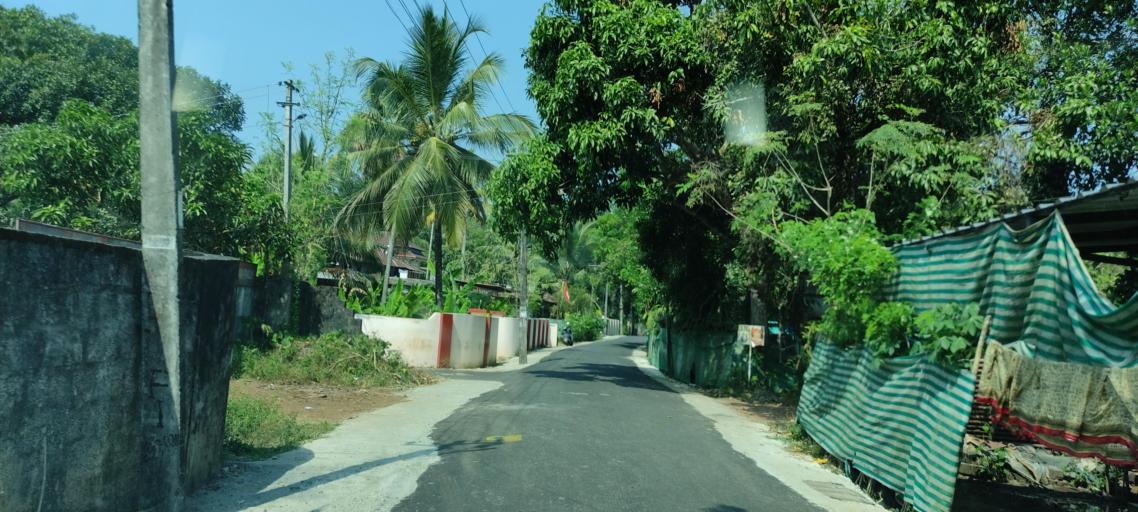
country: IN
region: Kerala
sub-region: Alappuzha
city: Alleppey
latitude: 9.5407
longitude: 76.3207
